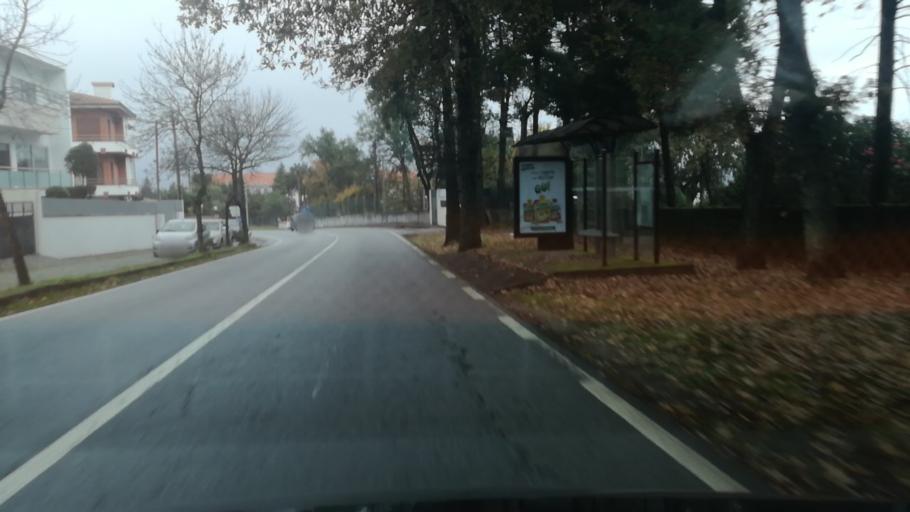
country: PT
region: Braga
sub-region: Braga
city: Braga
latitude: 41.5347
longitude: -8.4043
